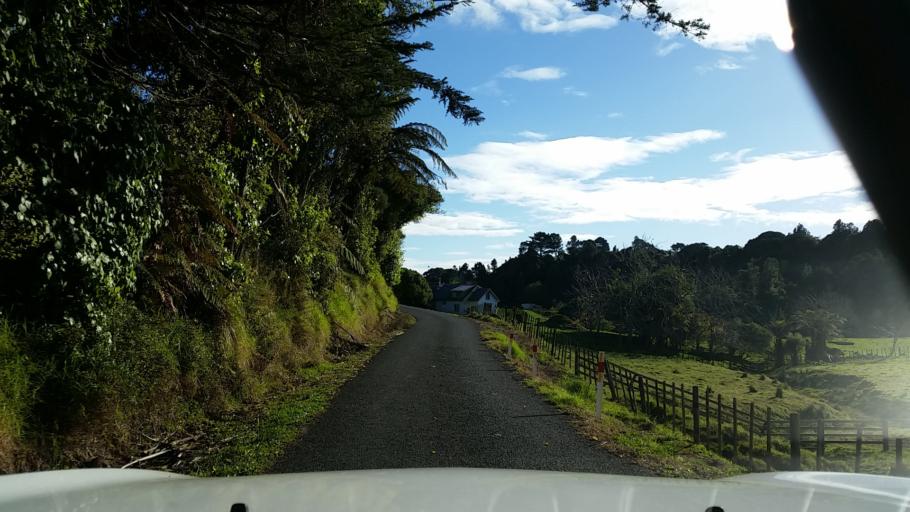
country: NZ
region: Taranaki
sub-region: New Plymouth District
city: Waitara
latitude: -38.9534
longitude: 174.4702
